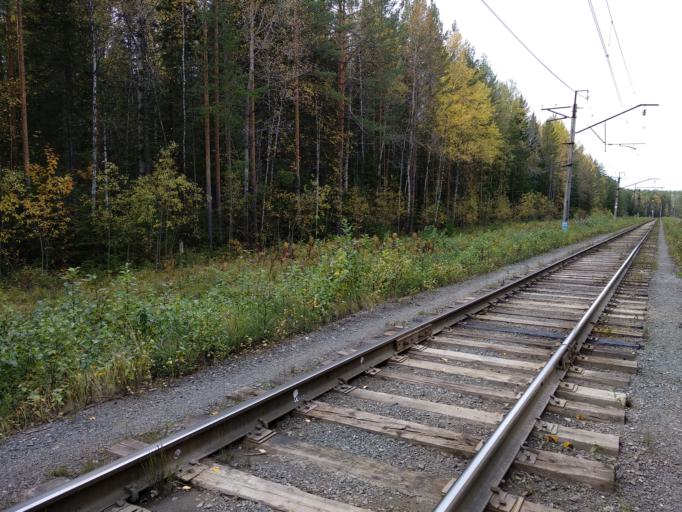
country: RU
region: Sverdlovsk
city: Krasnotur'insk
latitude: 59.7379
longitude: 60.1710
